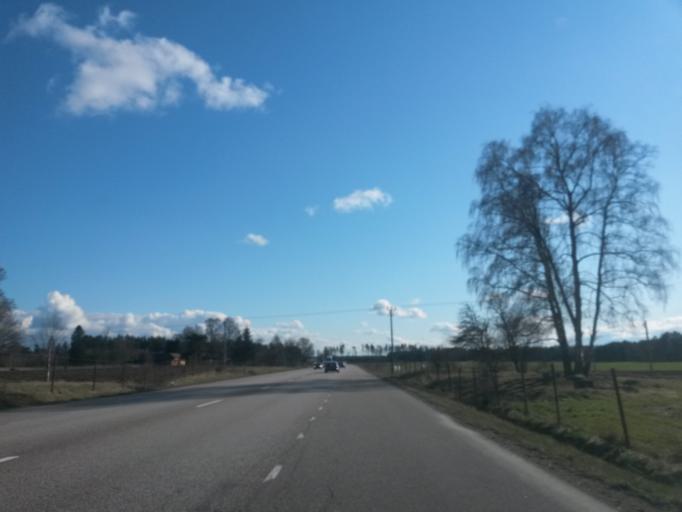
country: SE
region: Vaestra Goetaland
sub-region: Vara Kommun
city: Vara
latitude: 58.2030
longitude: 12.8988
